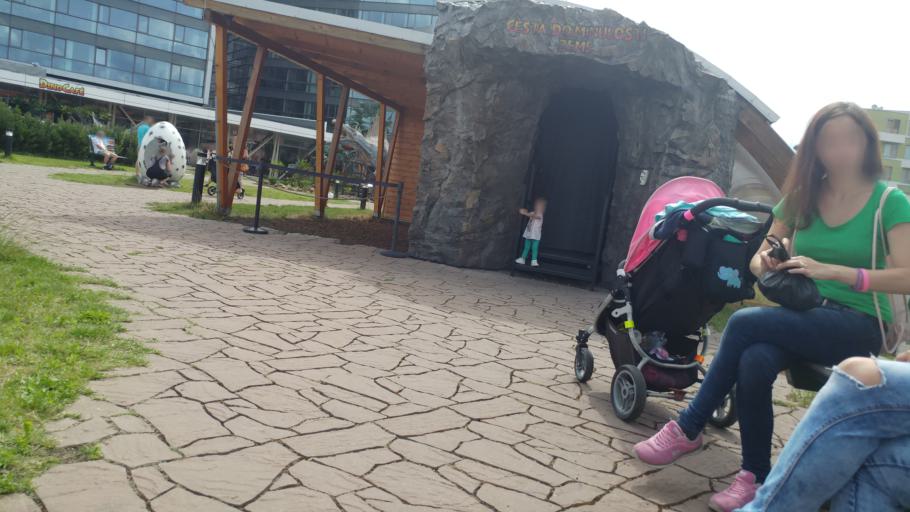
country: CZ
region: Praha
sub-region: Praha 8
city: Liben
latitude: 50.1046
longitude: 14.4904
